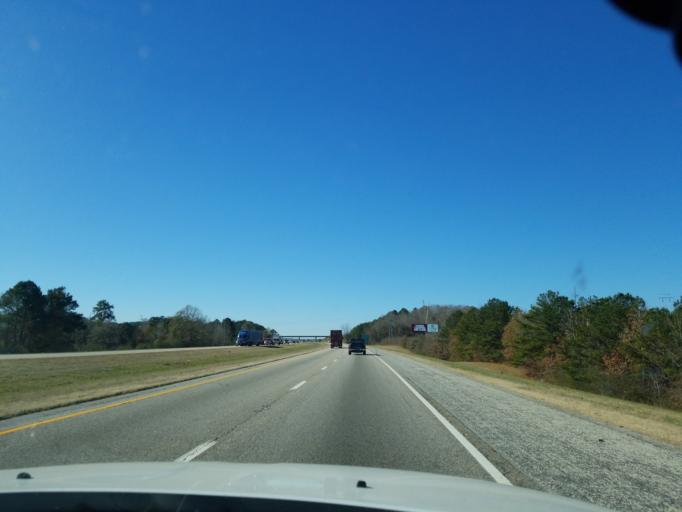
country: US
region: Alabama
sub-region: Jefferson County
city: Bessemer
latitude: 33.3343
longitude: -86.9736
